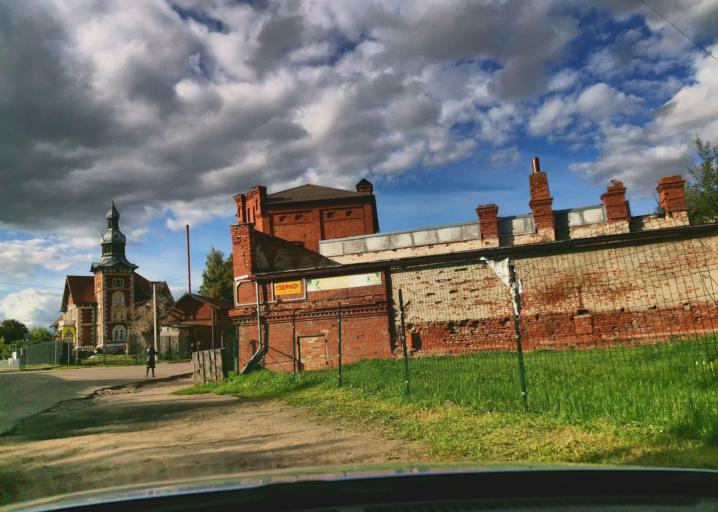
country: RU
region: Kaliningrad
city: Chernyakhovsk
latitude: 54.6408
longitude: 21.8038
